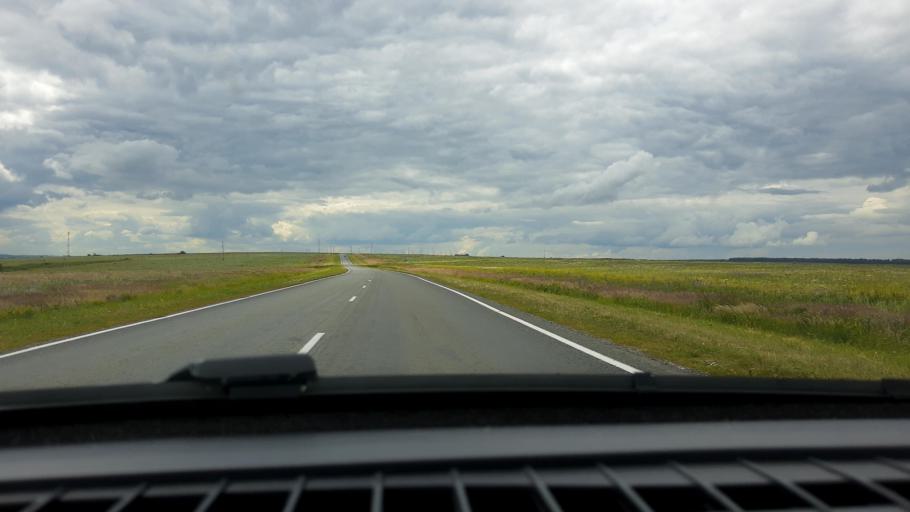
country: RU
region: Nizjnij Novgorod
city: Sergach
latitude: 55.5528
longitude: 45.5555
